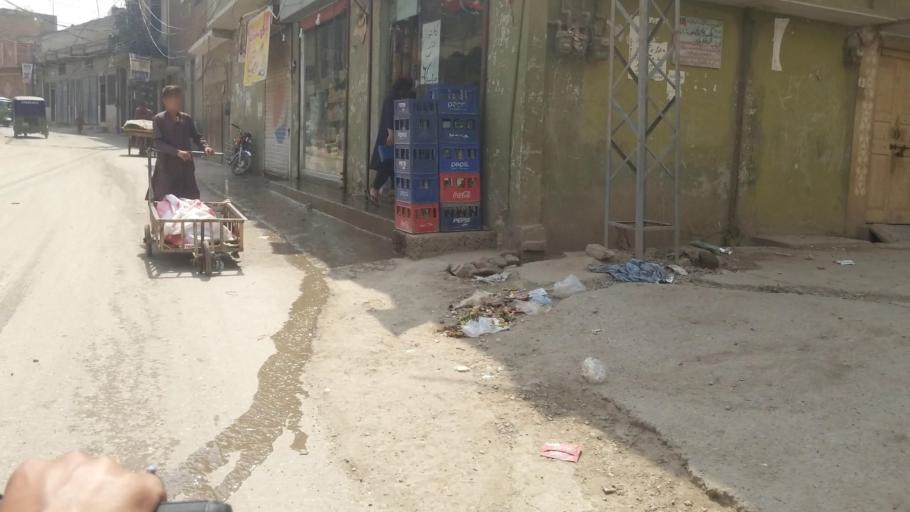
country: PK
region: Khyber Pakhtunkhwa
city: Peshawar
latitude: 33.9838
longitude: 71.5355
